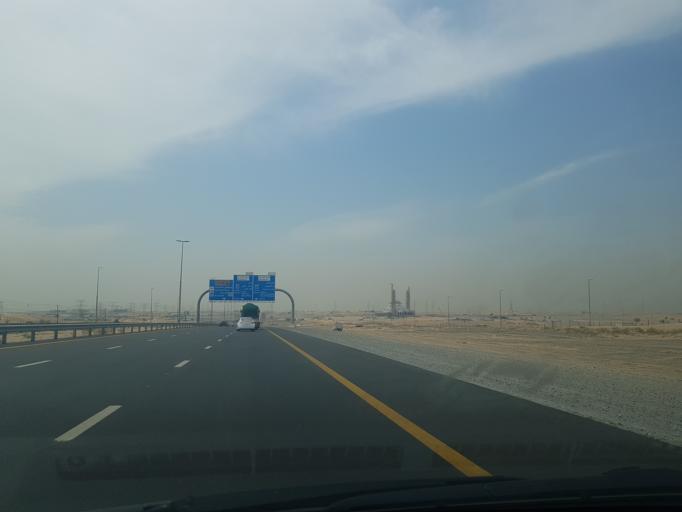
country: AE
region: Ash Shariqah
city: Sharjah
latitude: 25.2325
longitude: 55.5820
